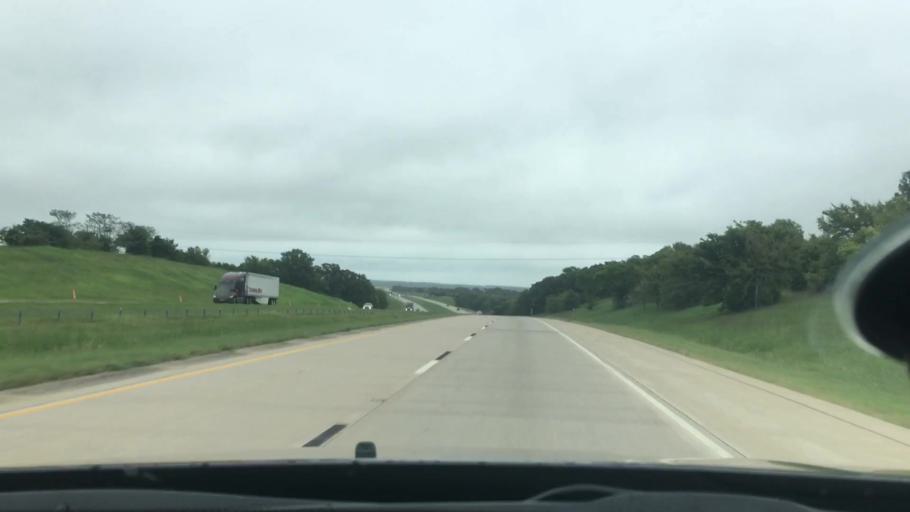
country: US
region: Oklahoma
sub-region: Okfuskee County
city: Okemah
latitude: 35.4274
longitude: -96.1582
